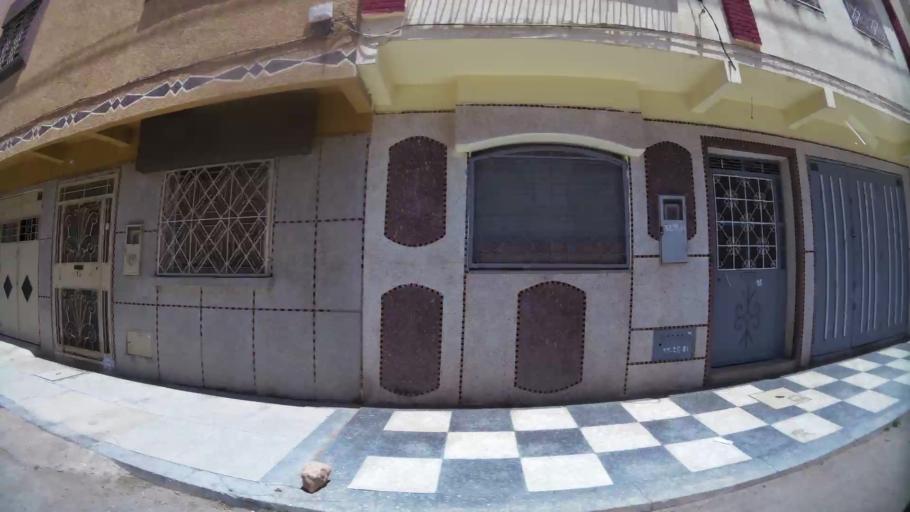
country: MA
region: Oriental
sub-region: Oujda-Angad
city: Oujda
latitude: 34.6986
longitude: -1.8946
